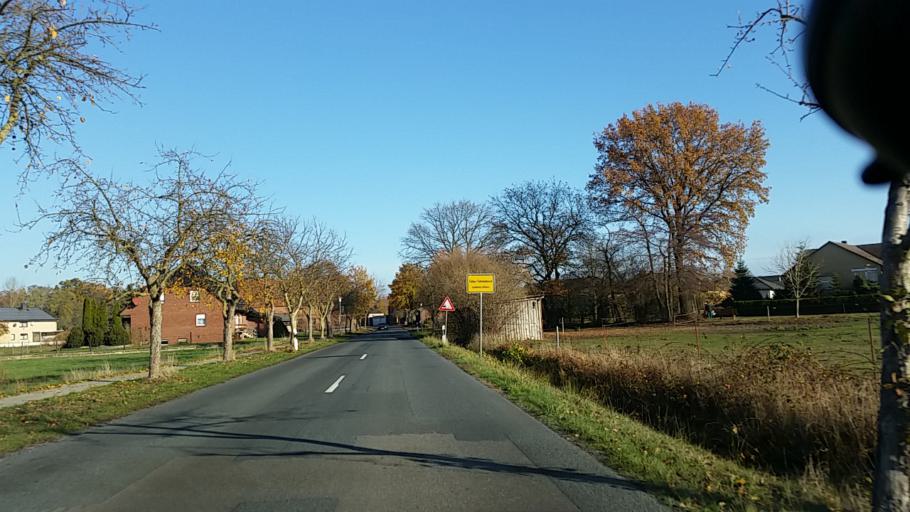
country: DE
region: Lower Saxony
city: Tulau
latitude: 52.5728
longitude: 10.8710
